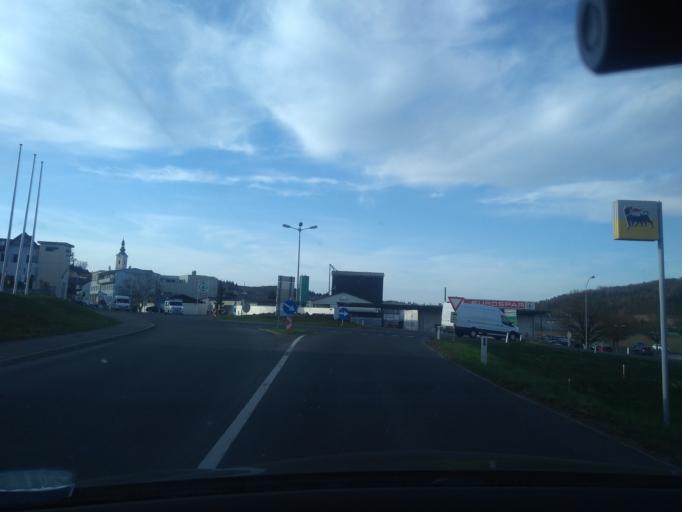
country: AT
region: Styria
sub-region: Politischer Bezirk Suedoststeiermark
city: Sankt Stefan im Rosental
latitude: 46.9010
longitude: 15.7132
